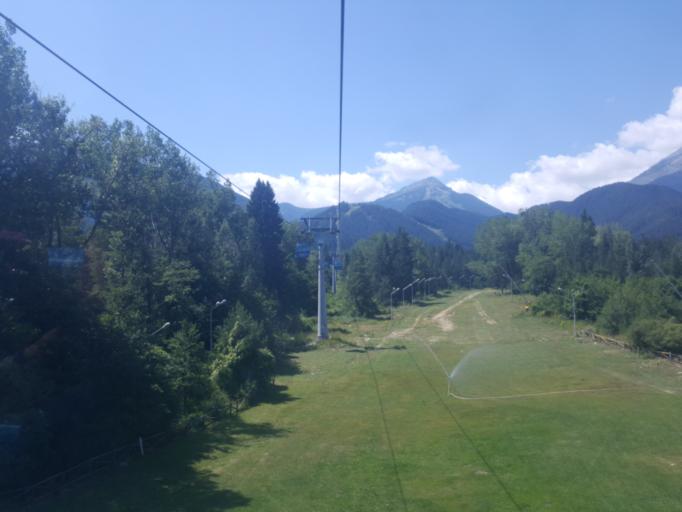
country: BG
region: Blagoevgrad
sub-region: Obshtina Bansko
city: Bansko
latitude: 41.8247
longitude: 23.4764
